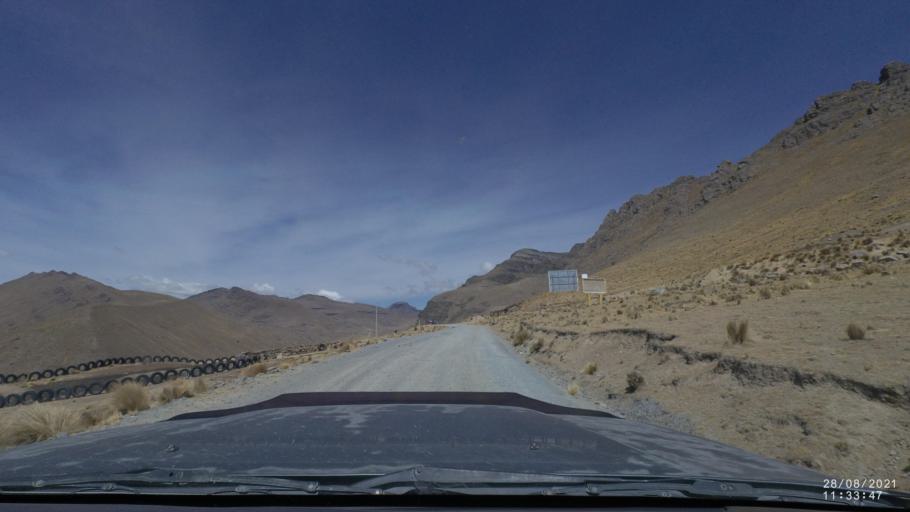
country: BO
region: Cochabamba
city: Sipe Sipe
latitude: -17.1878
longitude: -66.3718
